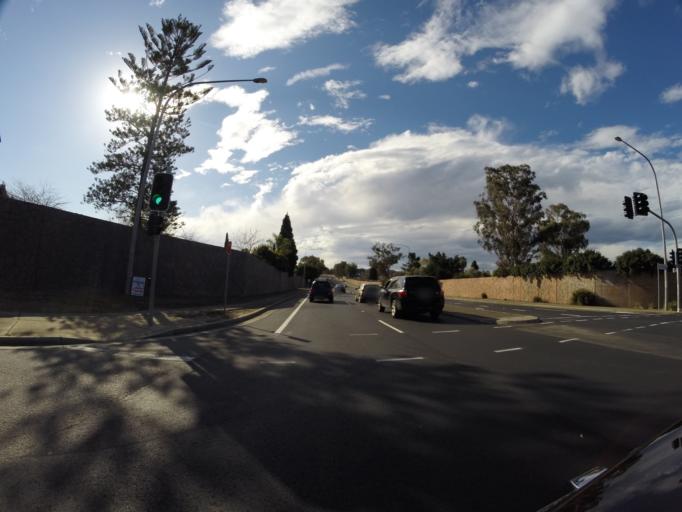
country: AU
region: New South Wales
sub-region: Fairfield
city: Cecil Park
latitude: -33.8688
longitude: 150.8700
